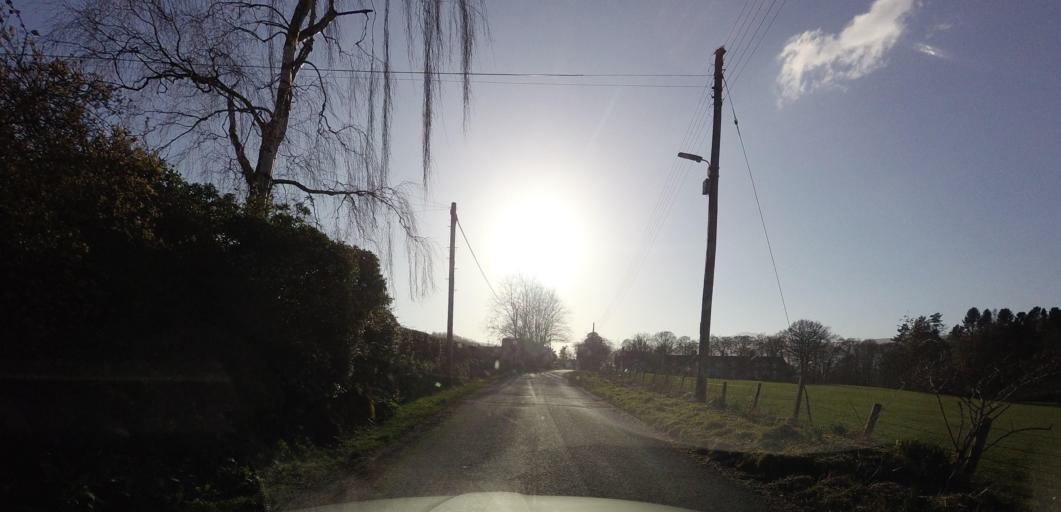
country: GB
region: Scotland
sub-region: Perth and Kinross
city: Aberfeldy
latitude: 56.5708
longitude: -4.0228
